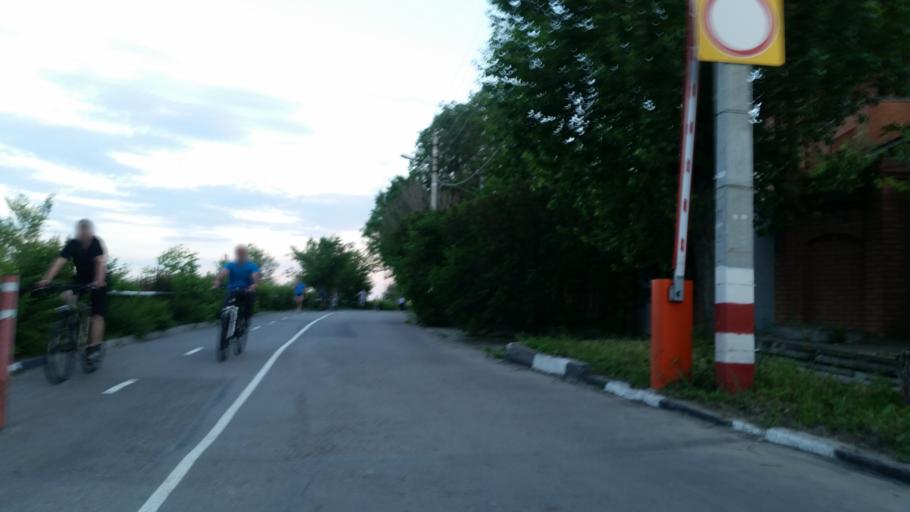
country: RU
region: Ulyanovsk
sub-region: Ulyanovskiy Rayon
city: Ulyanovsk
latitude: 54.3242
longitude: 48.4096
